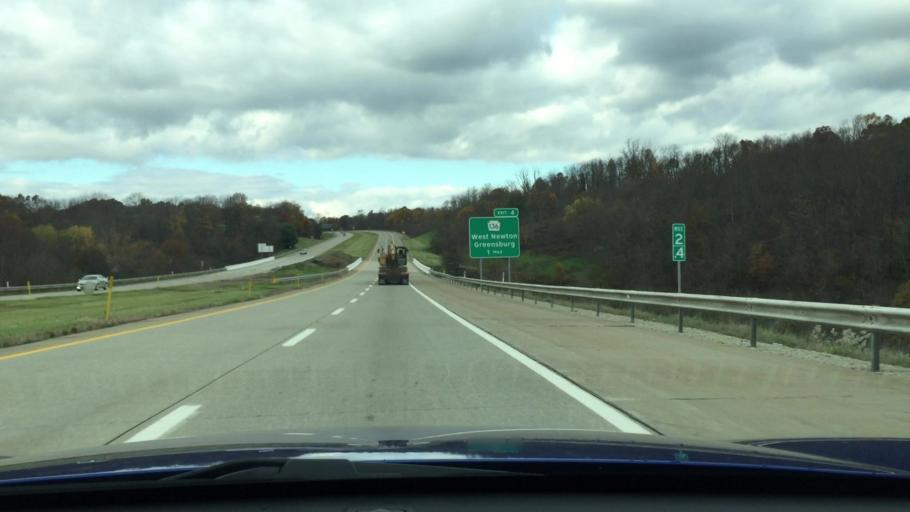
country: US
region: Pennsylvania
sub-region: Westmoreland County
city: New Stanton
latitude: 40.2563
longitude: -79.6127
